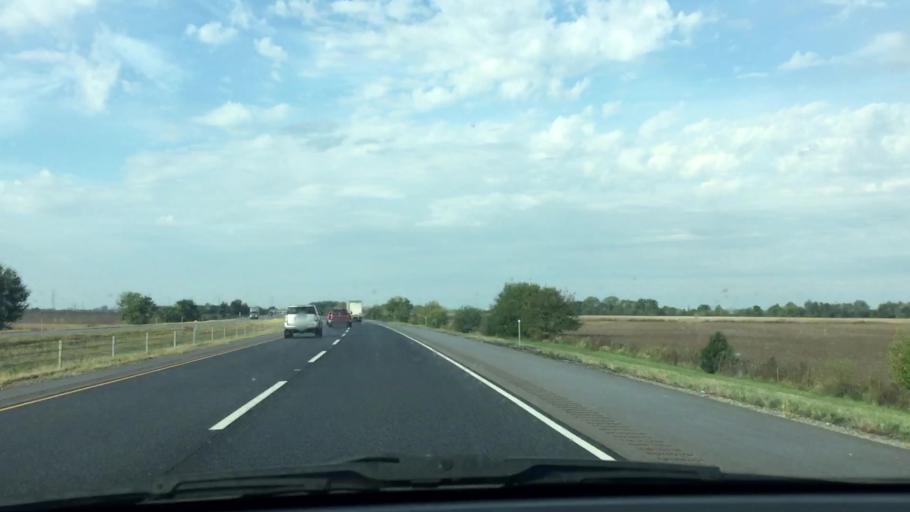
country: US
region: Illinois
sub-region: Lee County
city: Dixon
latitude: 41.7786
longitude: -89.5677
